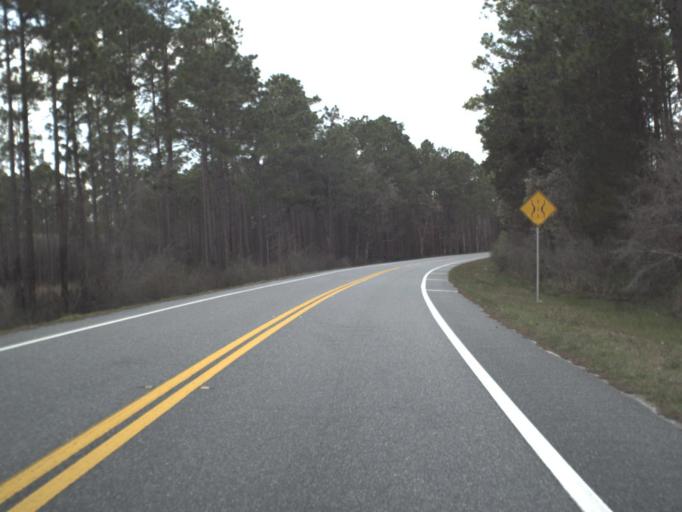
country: US
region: Florida
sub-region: Franklin County
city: Apalachicola
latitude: 29.8493
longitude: -84.9720
